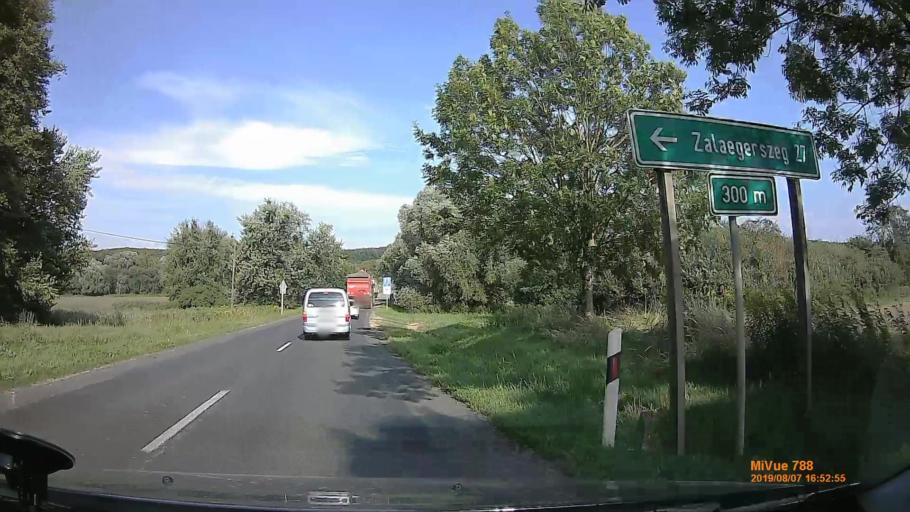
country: HU
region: Zala
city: Lenti
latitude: 46.6858
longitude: 16.6989
